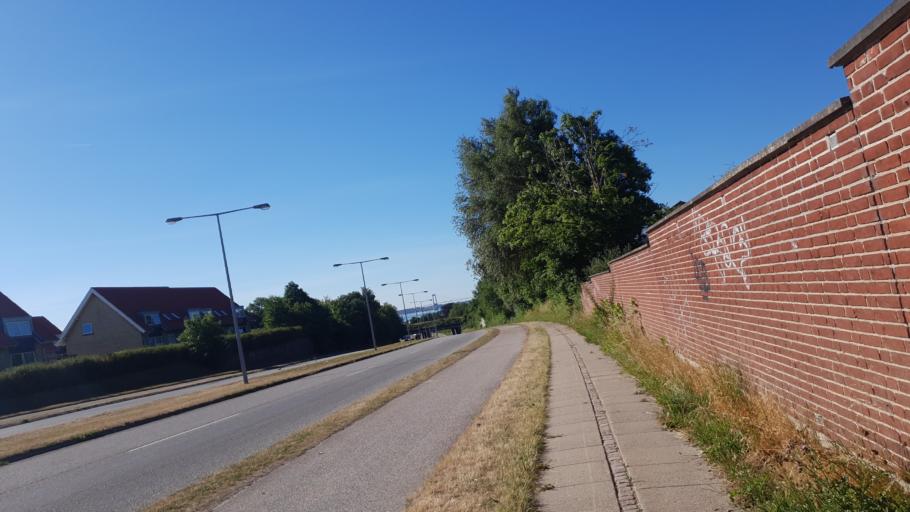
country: DK
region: South Denmark
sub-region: Fredericia Kommune
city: Fredericia
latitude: 55.5616
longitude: 9.7240
